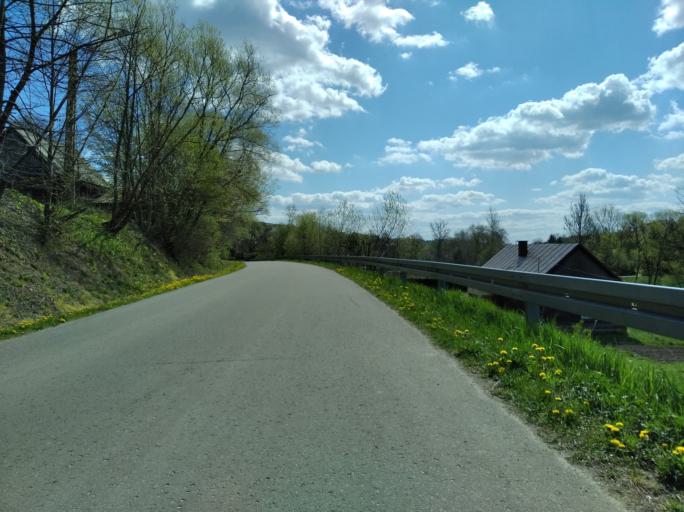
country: PL
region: Subcarpathian Voivodeship
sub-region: Powiat brzozowski
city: Wesola
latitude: 49.8027
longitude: 22.0945
